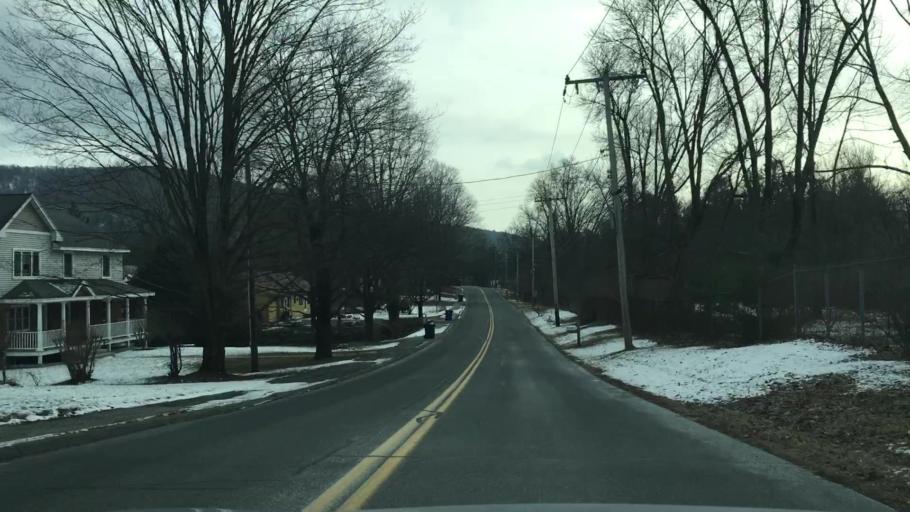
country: US
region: Massachusetts
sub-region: Berkshire County
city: Lee
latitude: 42.2953
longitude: -73.2475
